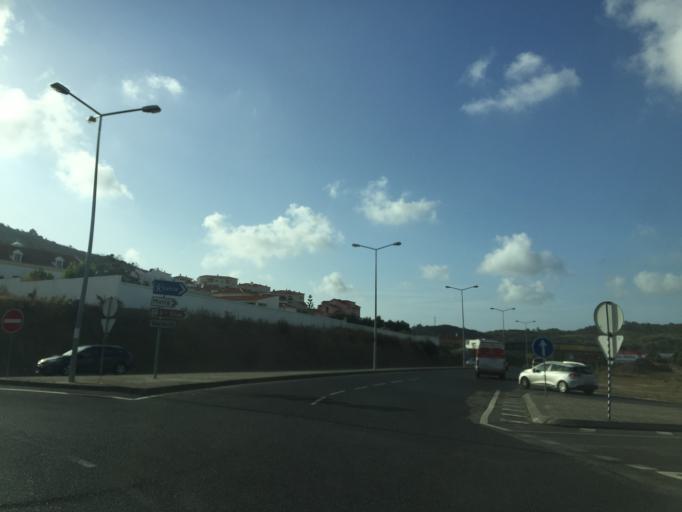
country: PT
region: Lisbon
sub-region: Torres Vedras
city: Torres Vedras
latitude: 39.0875
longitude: -9.2638
